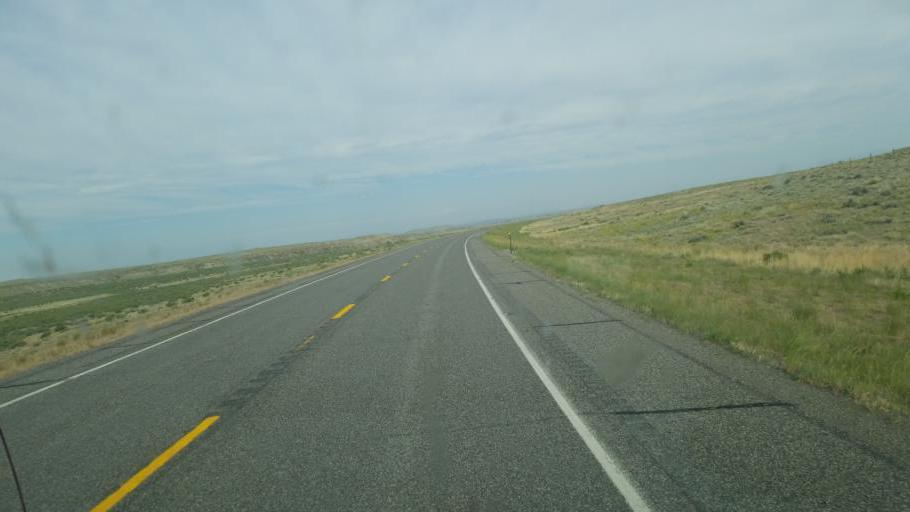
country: US
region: Wyoming
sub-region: Fremont County
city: Riverton
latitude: 43.2235
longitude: -108.0418
